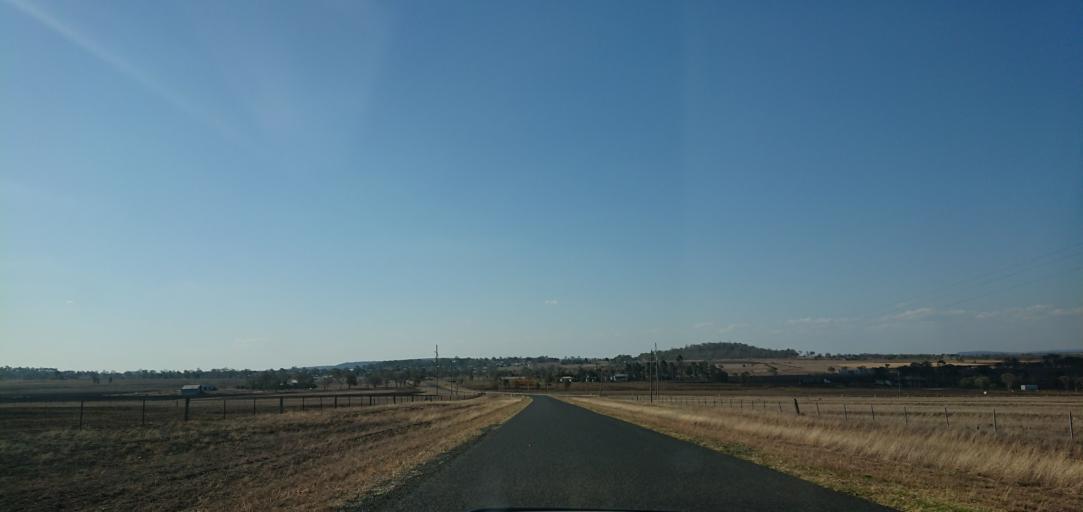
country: AU
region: Queensland
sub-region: Toowoomba
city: Westbrook
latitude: -27.6977
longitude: 151.7149
